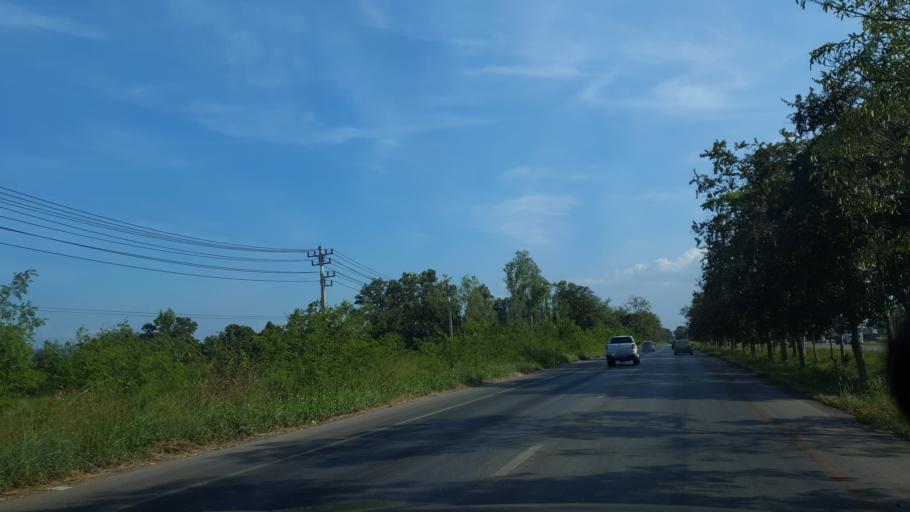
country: TH
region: Surat Thani
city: Phunphin
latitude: 9.0154
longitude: 99.1835
